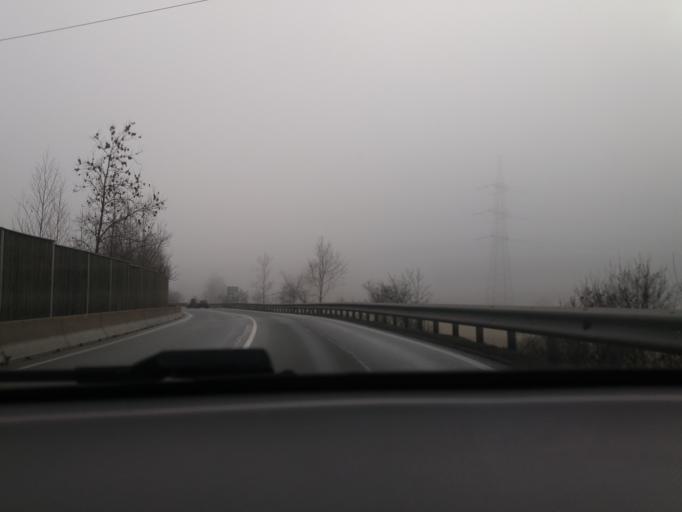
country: AT
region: Salzburg
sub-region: Politischer Bezirk Zell am See
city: Bruck an der Grossglocknerstrasse
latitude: 47.2831
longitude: 12.8118
